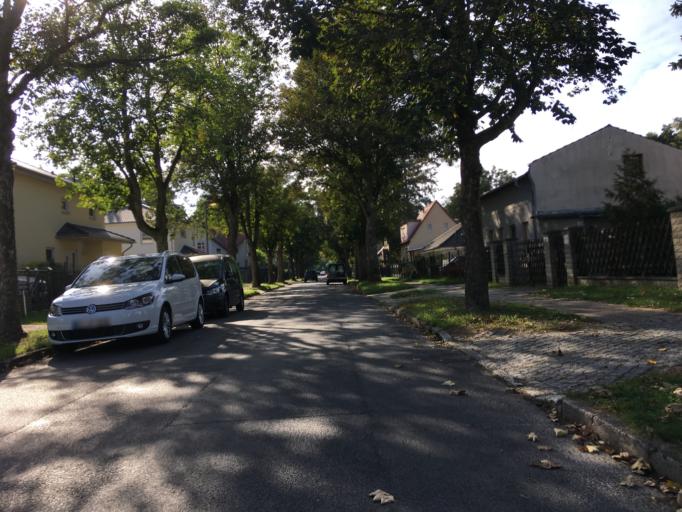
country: DE
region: Brandenburg
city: Neuenhagen
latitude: 52.5161
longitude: 13.6886
